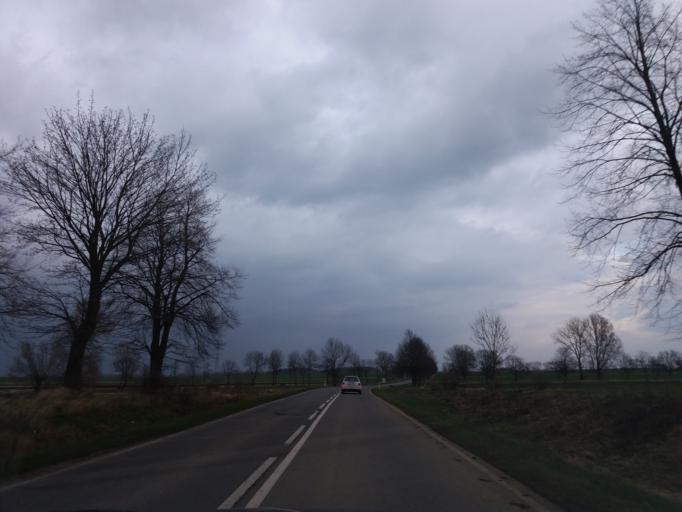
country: PL
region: West Pomeranian Voivodeship
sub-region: Powiat pyrzycki
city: Przelewice
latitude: 53.1436
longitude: 15.0036
